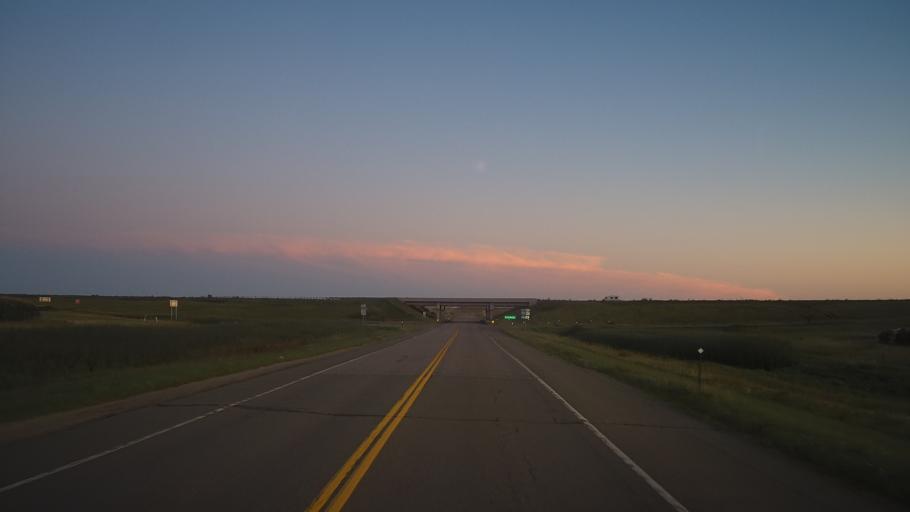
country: US
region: South Dakota
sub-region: Lyman County
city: Kennebec
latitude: 43.8666
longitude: -99.6061
